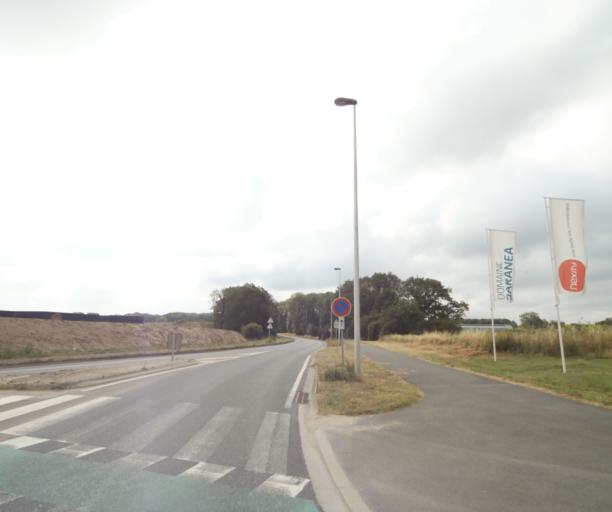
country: FR
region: Centre
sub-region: Departement du Loiret
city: Saran
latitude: 47.9601
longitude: 1.8806
